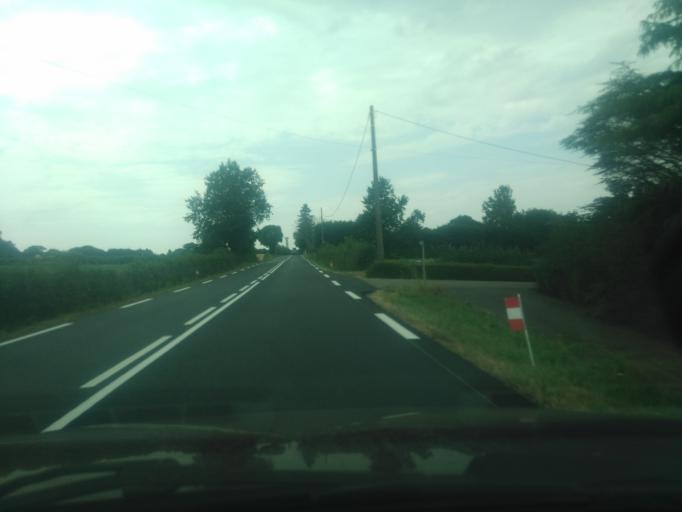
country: FR
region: Poitou-Charentes
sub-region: Departement des Deux-Sevres
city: Secondigny
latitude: 46.6141
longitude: -0.4413
